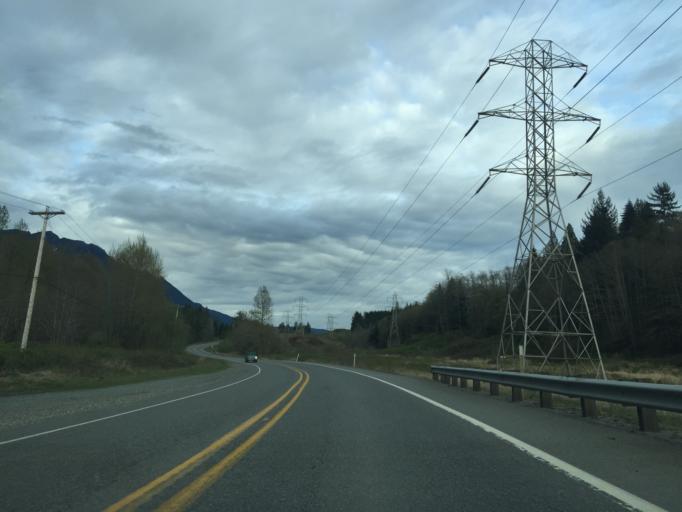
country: US
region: Washington
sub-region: Snohomish County
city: Arlington Heights
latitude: 48.2691
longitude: -121.8797
